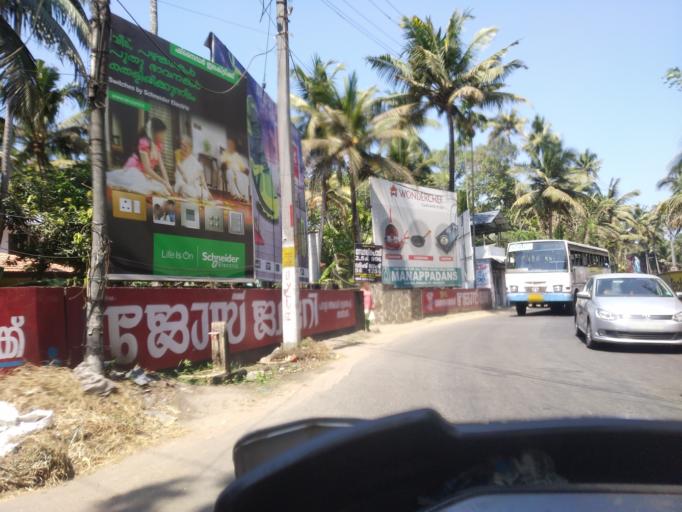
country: IN
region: Kerala
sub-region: Thrissur District
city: Kodungallur
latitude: 10.1681
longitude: 76.2128
